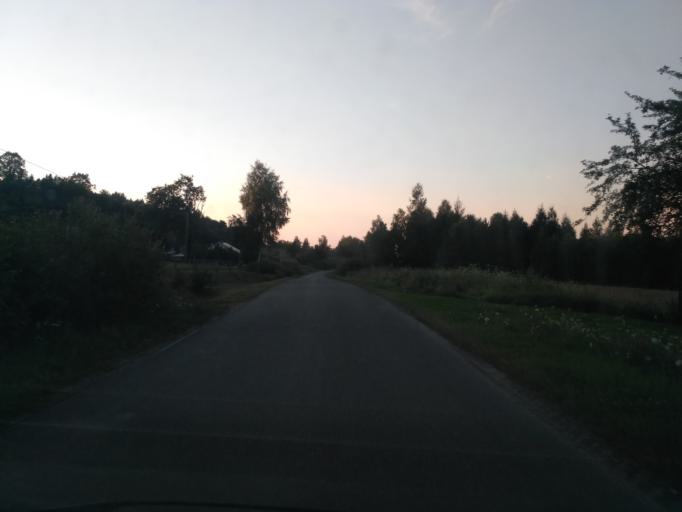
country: PL
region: Subcarpathian Voivodeship
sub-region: Powiat strzyzowski
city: Wysoka Strzyzowska
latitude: 49.7970
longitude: 21.7534
